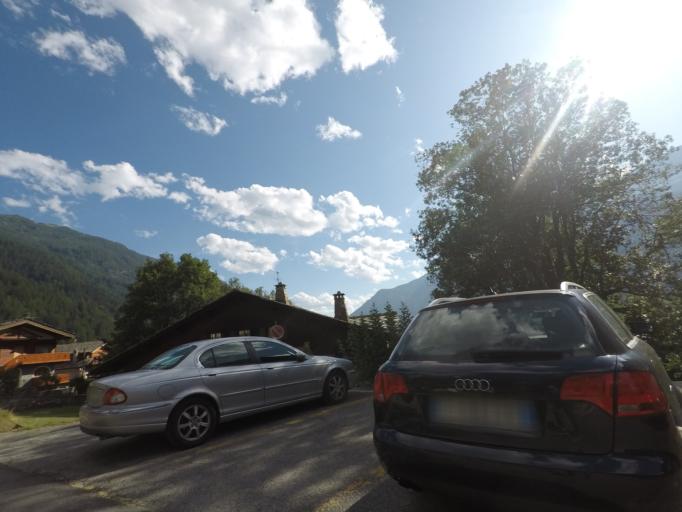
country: IT
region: Aosta Valley
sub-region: Valle d'Aosta
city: Valtournenche
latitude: 45.8758
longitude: 7.6258
